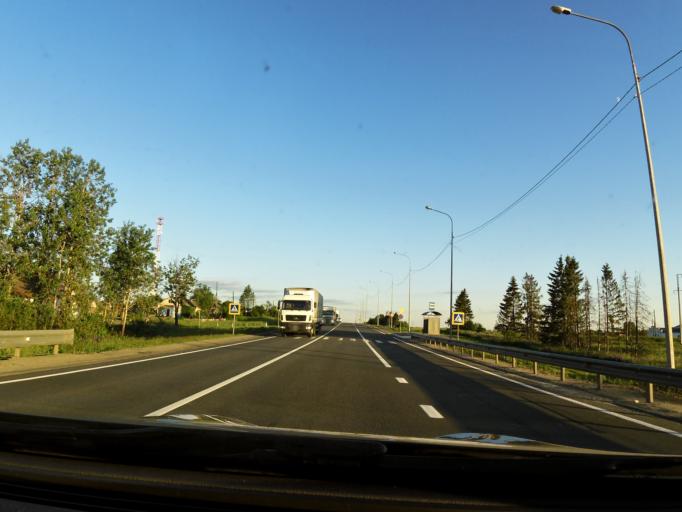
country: RU
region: Vologda
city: Gryazovets
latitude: 58.7085
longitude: 40.2971
